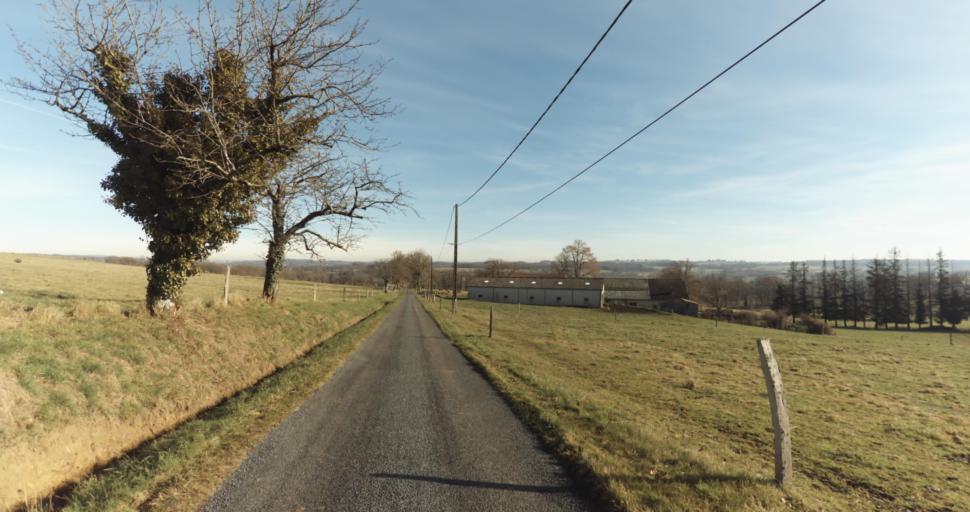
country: FR
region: Limousin
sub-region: Departement de la Haute-Vienne
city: Aixe-sur-Vienne
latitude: 45.7727
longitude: 1.1176
